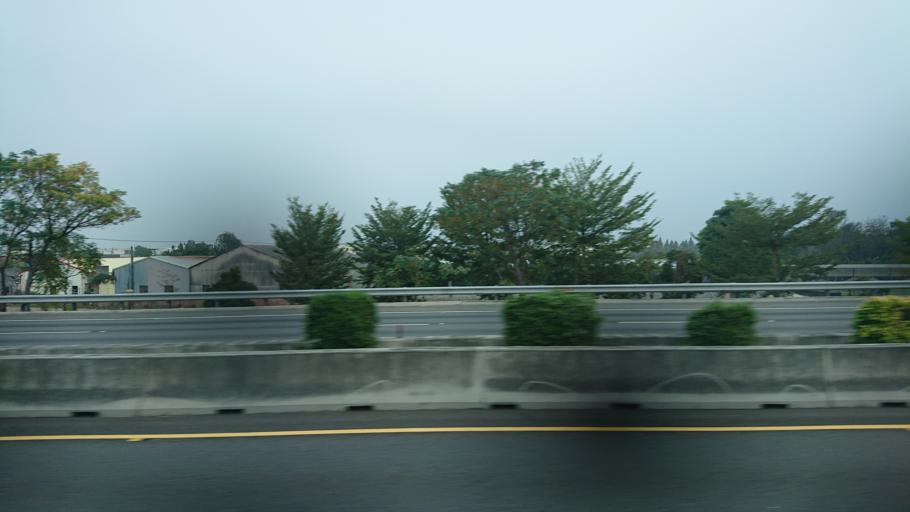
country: TW
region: Taiwan
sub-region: Nantou
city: Nantou
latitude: 23.9067
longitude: 120.4979
